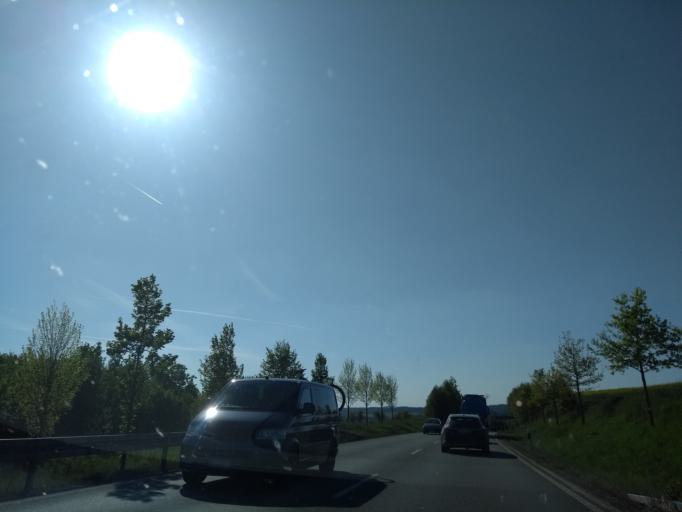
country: DE
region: Hesse
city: Frankenberg
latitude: 51.0419
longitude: 8.7800
